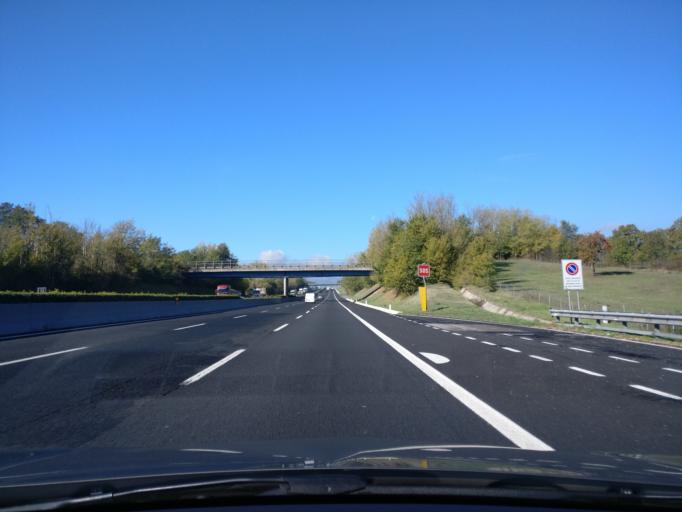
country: IT
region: Latium
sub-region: Provincia di Frosinone
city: Pofi
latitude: 41.5515
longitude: 13.4498
